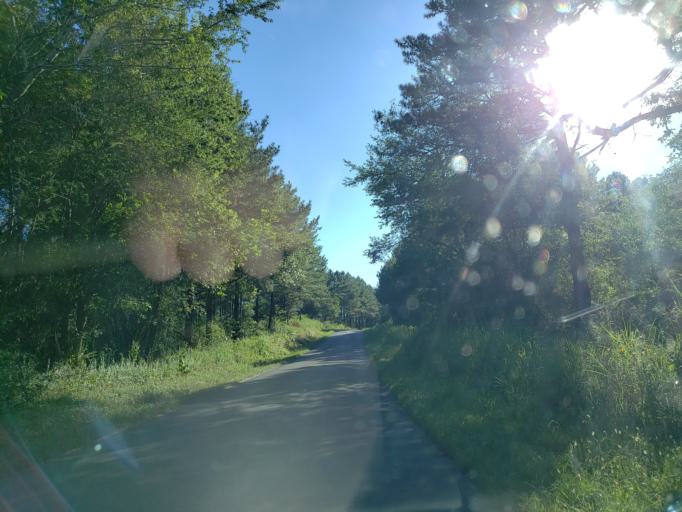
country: US
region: Georgia
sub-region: Polk County
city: Aragon
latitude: 34.1213
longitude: -85.0284
